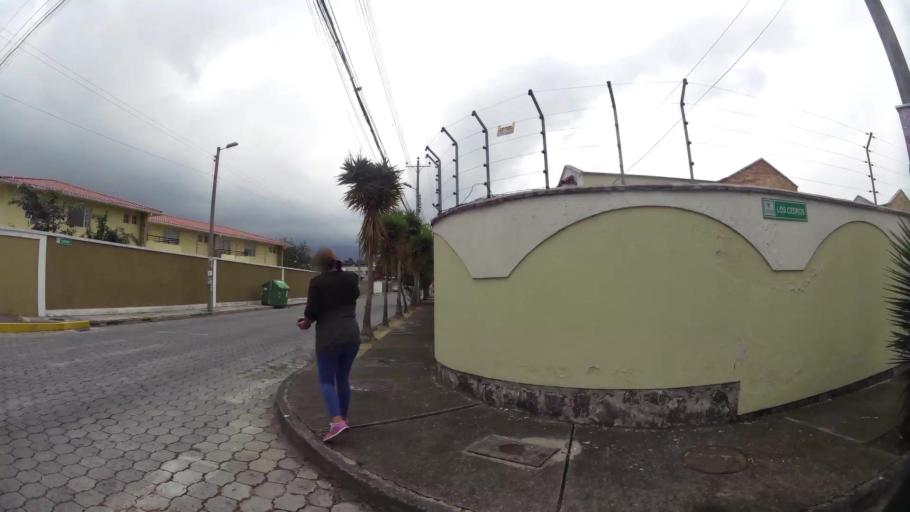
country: EC
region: Pichincha
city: Sangolqui
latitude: -0.3126
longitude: -78.4623
